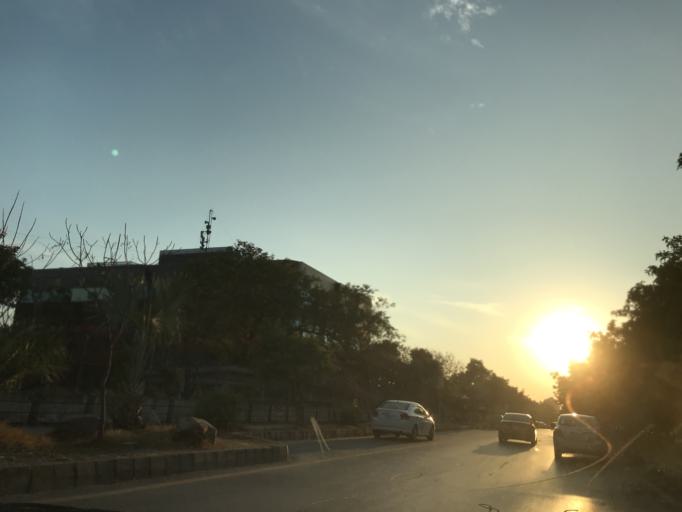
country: PK
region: Islamabad
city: Islamabad
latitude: 33.7144
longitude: 73.0395
